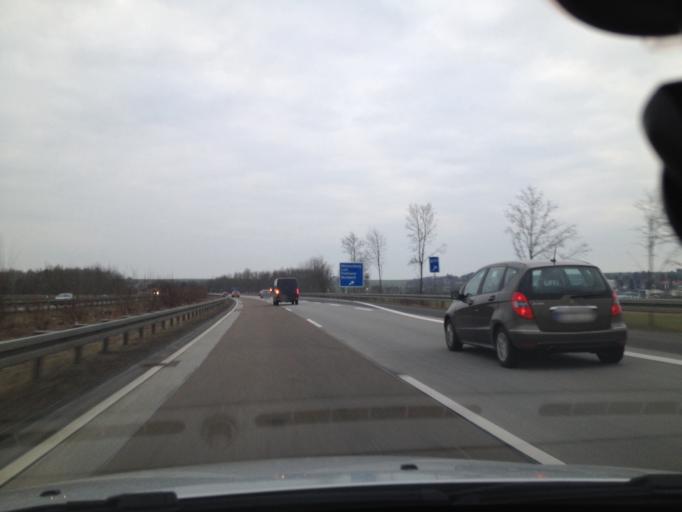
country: DE
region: Hesse
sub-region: Regierungsbezirk Darmstadt
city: Munzenberg
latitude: 50.4707
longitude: 8.7664
